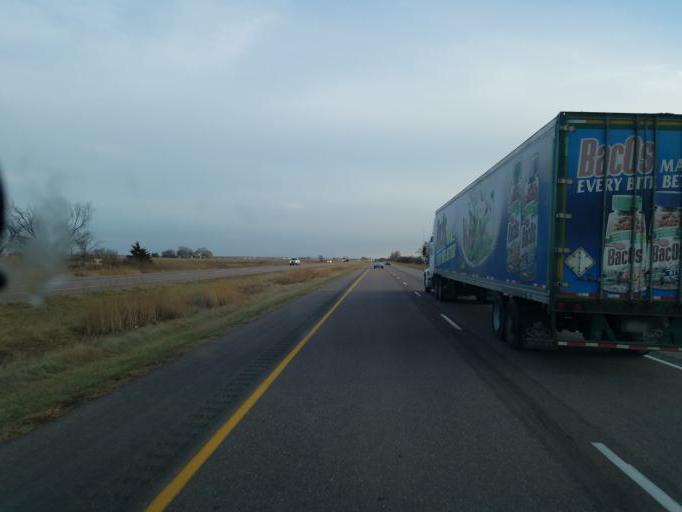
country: US
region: Iowa
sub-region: Monona County
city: Onawa
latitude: 42.0699
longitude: -96.1678
